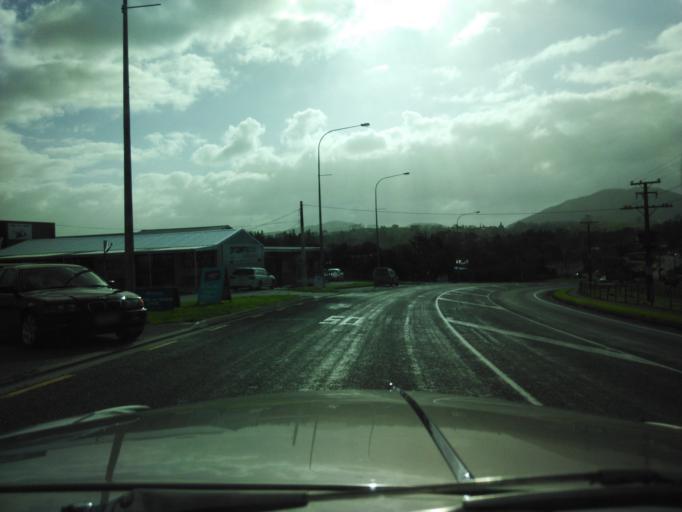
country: NZ
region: Auckland
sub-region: Auckland
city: Wellsford
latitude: -36.1650
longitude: 174.4435
